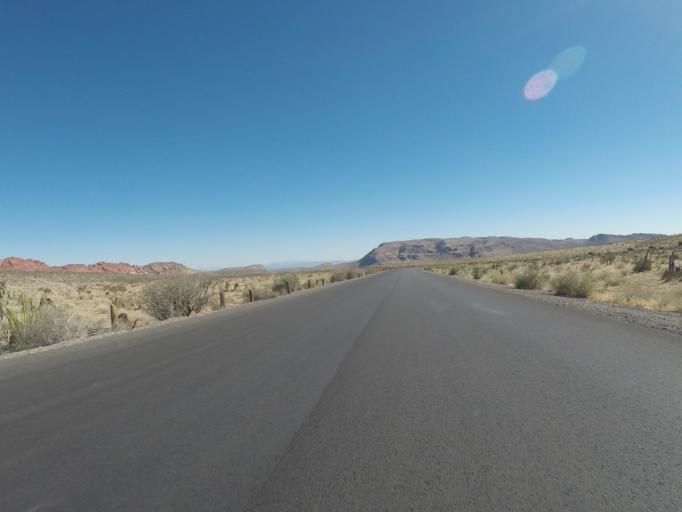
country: US
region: Nevada
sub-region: Clark County
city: Summerlin South
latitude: 36.1412
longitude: -115.4682
